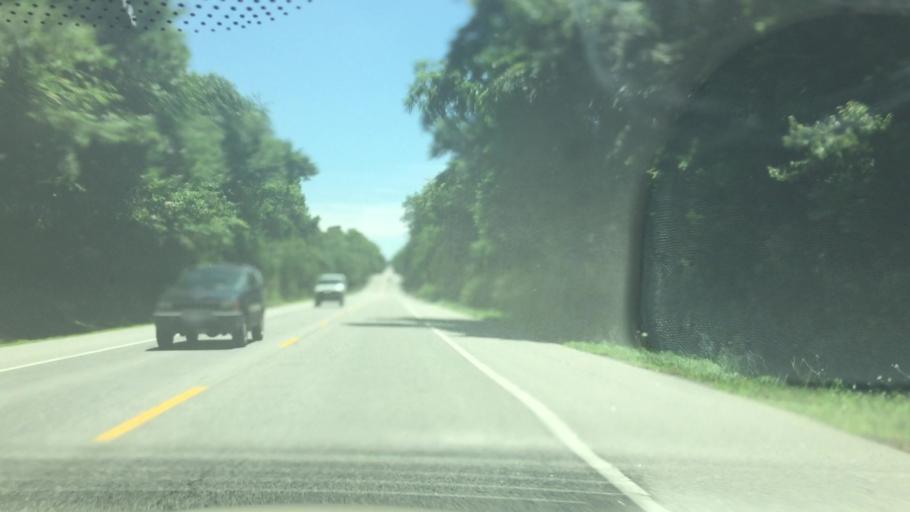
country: US
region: Maryland
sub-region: Cecil County
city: Rising Sun
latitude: 39.6594
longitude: -76.0751
